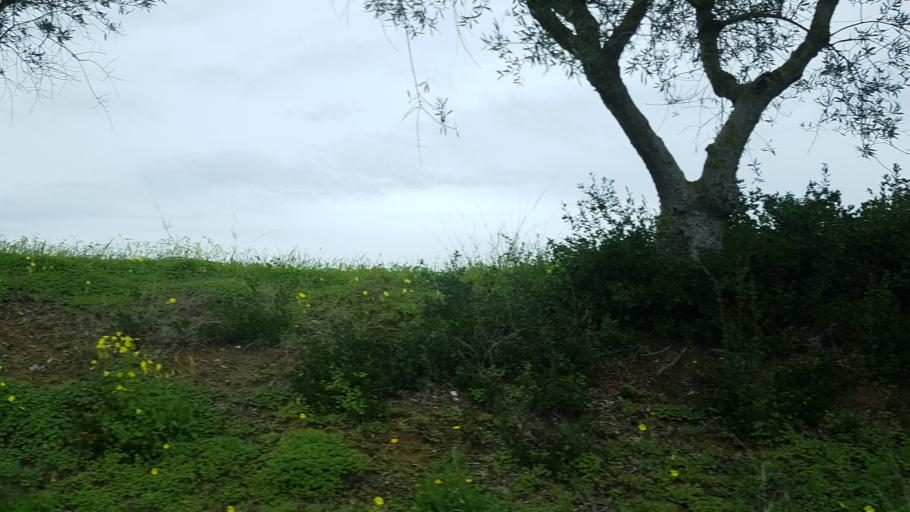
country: PT
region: Lisbon
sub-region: Alenquer
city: Carregado
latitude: 39.0396
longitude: -8.9746
